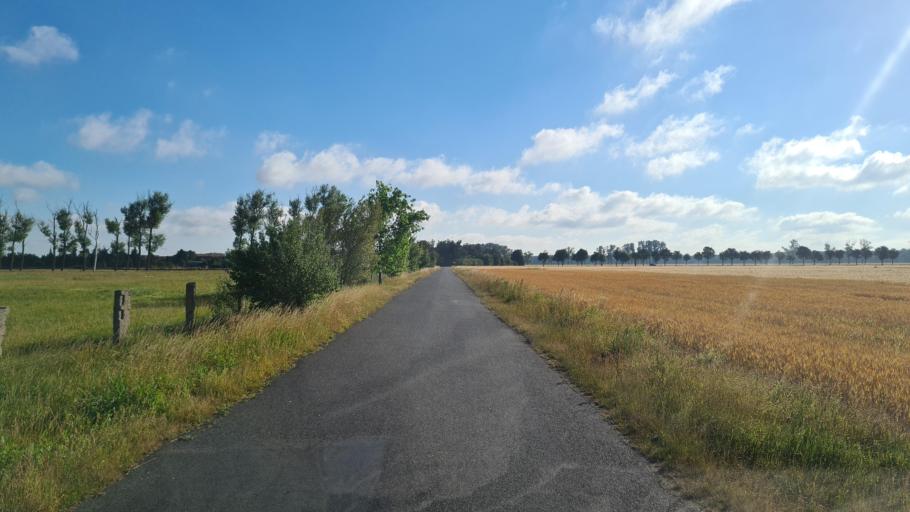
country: DE
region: Saxony
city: Beilrode
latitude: 51.6308
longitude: 13.1169
